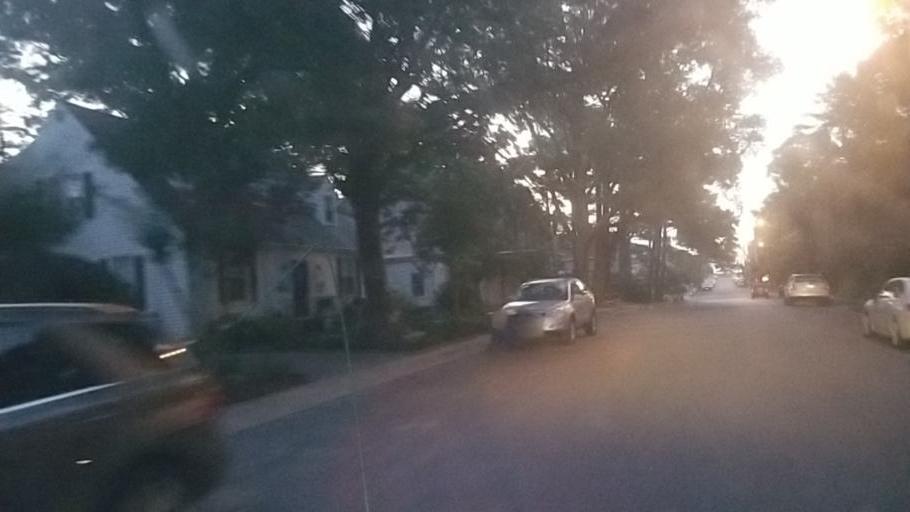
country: US
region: Delaware
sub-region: Sussex County
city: Rehoboth Beach
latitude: 38.7102
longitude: -75.0794
